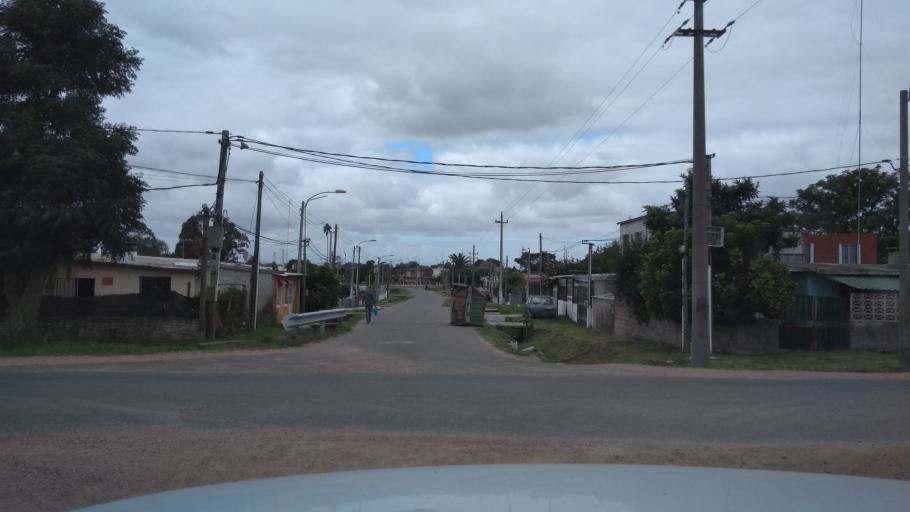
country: UY
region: Canelones
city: Toledo
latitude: -34.7784
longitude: -56.1372
